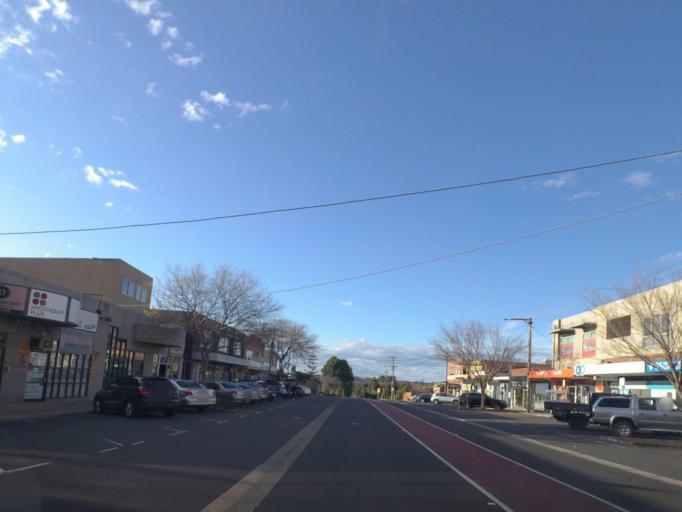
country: AU
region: Victoria
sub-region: Boroondara
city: Balwyn North
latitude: -37.7875
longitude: 145.0862
